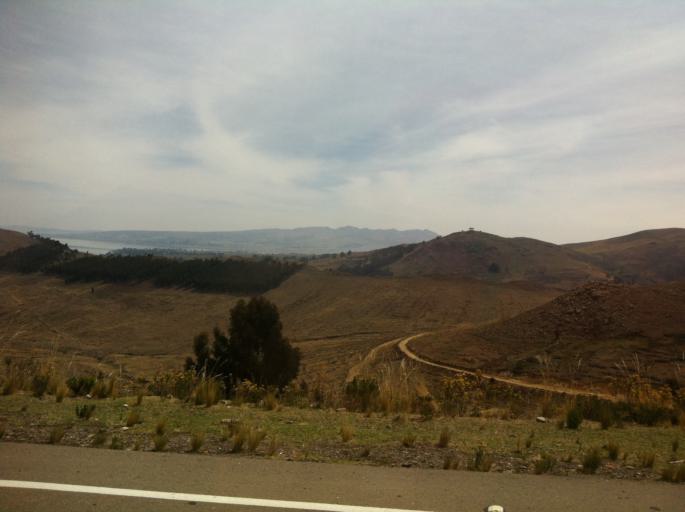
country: PE
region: Puno
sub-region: Yunguyo
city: Yunguyo
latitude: -16.1888
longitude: -68.9772
